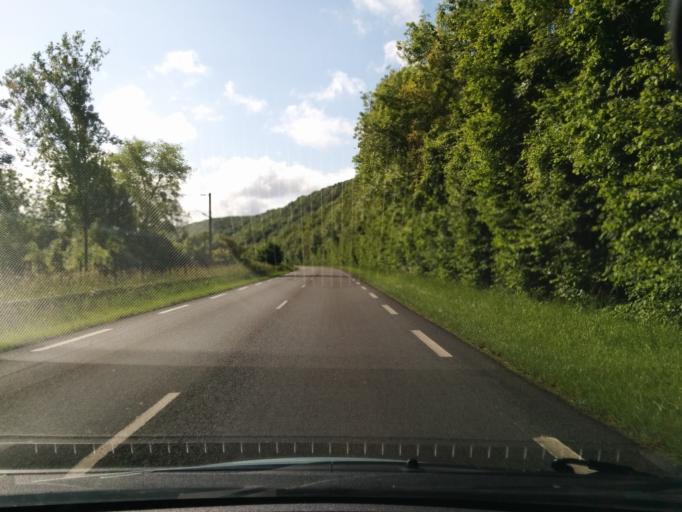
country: FR
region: Ile-de-France
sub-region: Departement des Yvelines
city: Bennecourt
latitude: 49.0420
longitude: 1.5348
